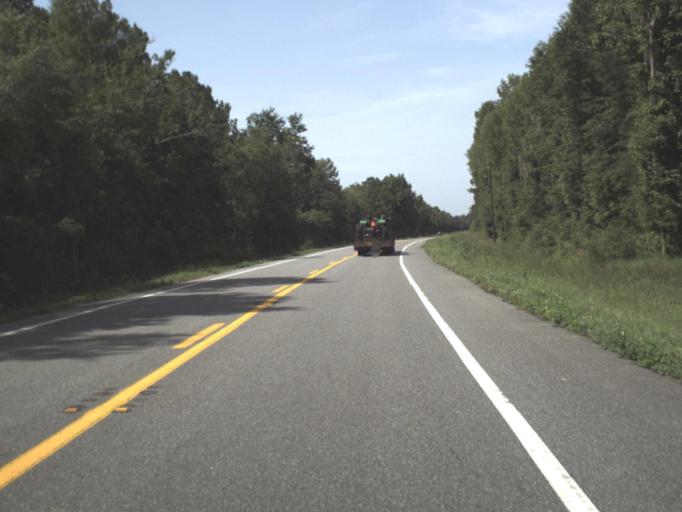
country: US
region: Florida
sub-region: Lafayette County
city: Mayo
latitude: 29.9891
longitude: -83.1976
